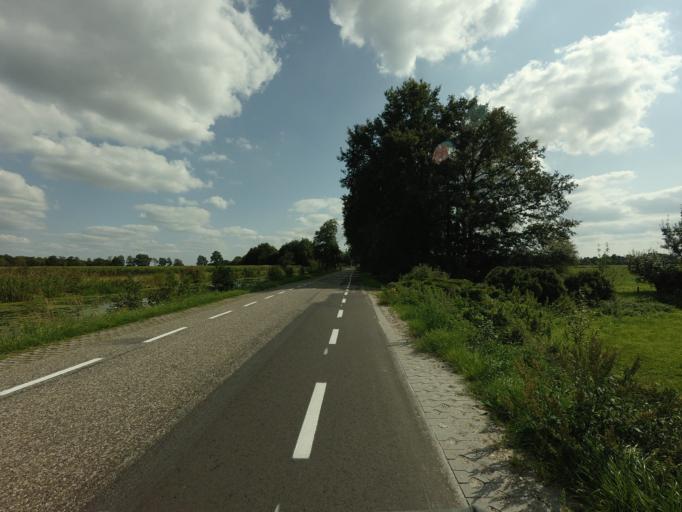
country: NL
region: Drenthe
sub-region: Gemeente Westerveld
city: Dwingeloo
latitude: 52.8623
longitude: 6.4637
